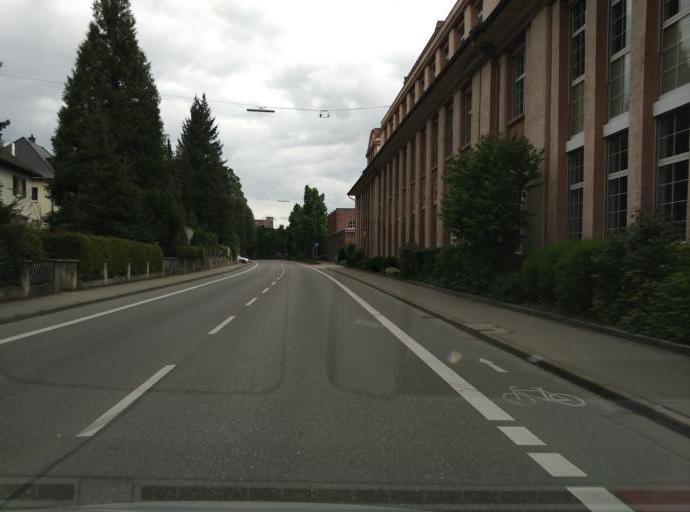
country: DE
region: Baden-Wuerttemberg
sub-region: Regierungsbezirk Stuttgart
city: Nurtingen
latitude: 48.6216
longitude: 9.3430
